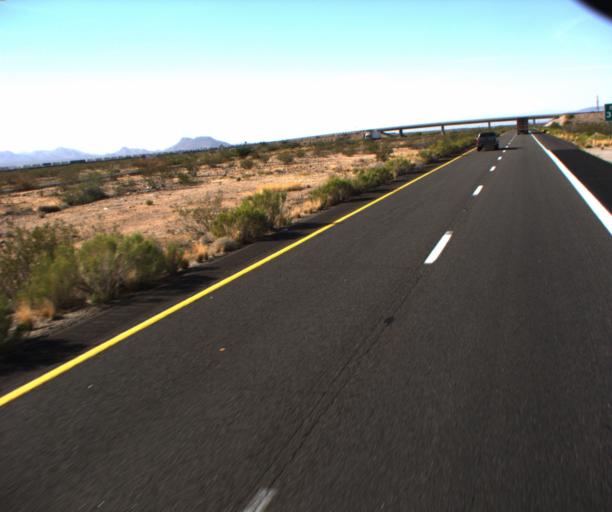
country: US
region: Arizona
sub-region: Mohave County
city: Kingman
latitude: 35.0369
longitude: -114.1302
